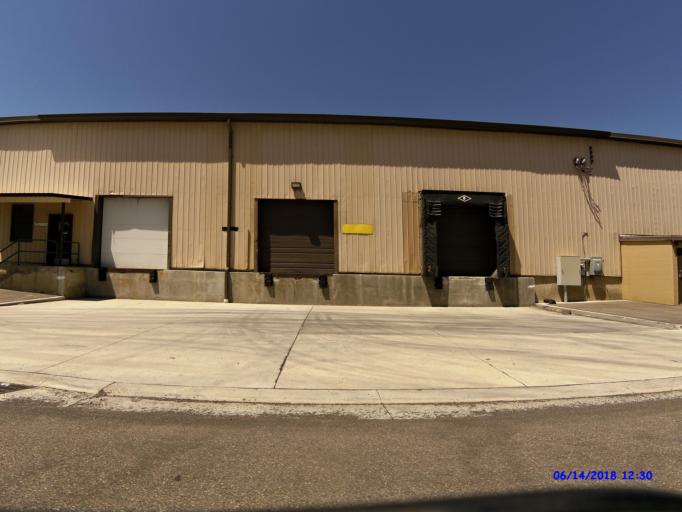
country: US
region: Utah
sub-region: Weber County
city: Marriott-Slaterville
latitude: 41.2598
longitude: -112.0026
